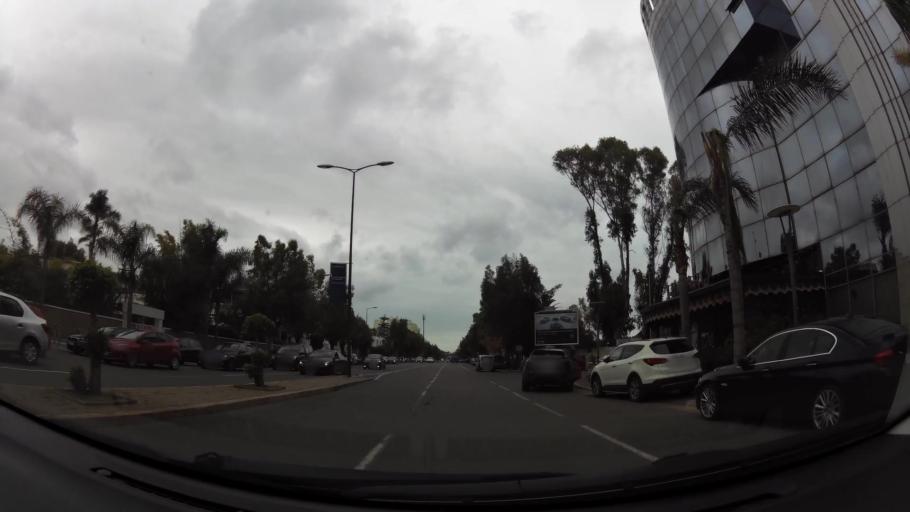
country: MA
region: Grand Casablanca
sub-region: Casablanca
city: Casablanca
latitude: 33.5883
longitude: -7.6449
